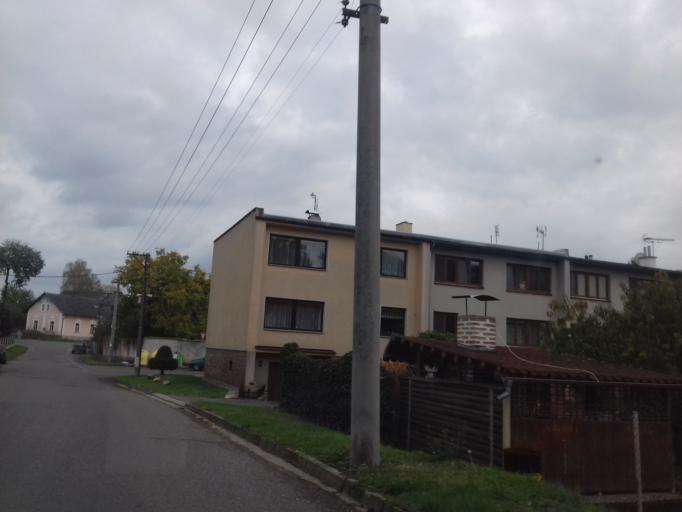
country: CZ
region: Pardubicky
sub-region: Okres Chrudim
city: Chrast
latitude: 49.9200
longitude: 15.9121
